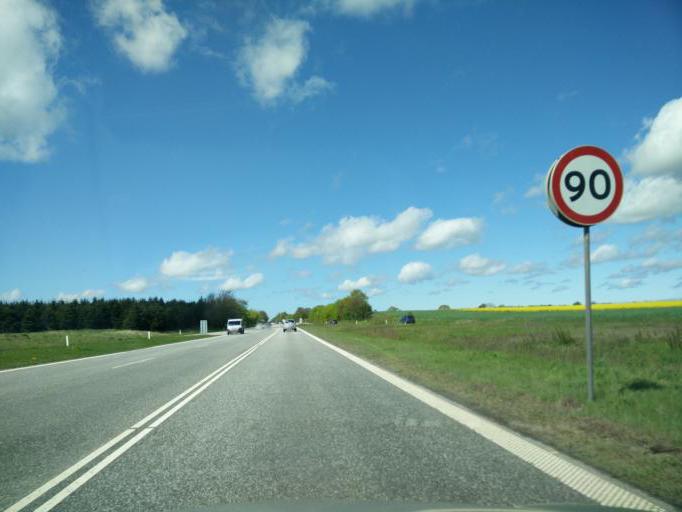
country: DK
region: Capital Region
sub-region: Hillerod Kommune
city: Hillerod
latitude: 55.9085
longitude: 12.2675
